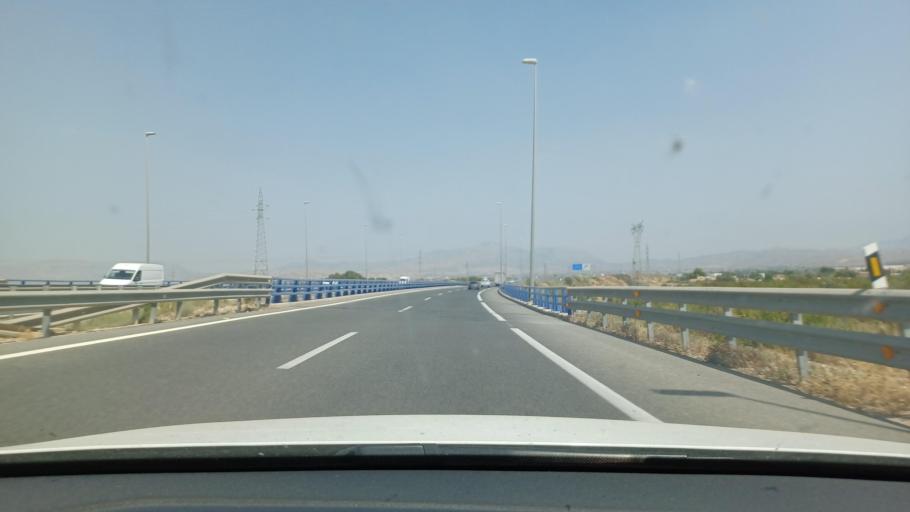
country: ES
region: Valencia
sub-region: Provincia de Alicante
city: San Vicent del Raspeig
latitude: 38.3883
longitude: -0.5445
